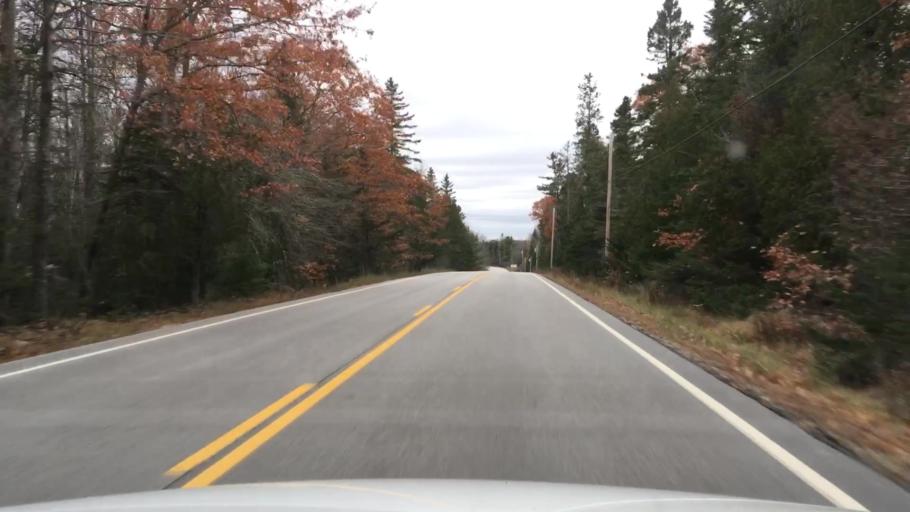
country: US
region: Maine
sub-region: Hancock County
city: Penobscot
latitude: 44.4906
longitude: -68.6433
